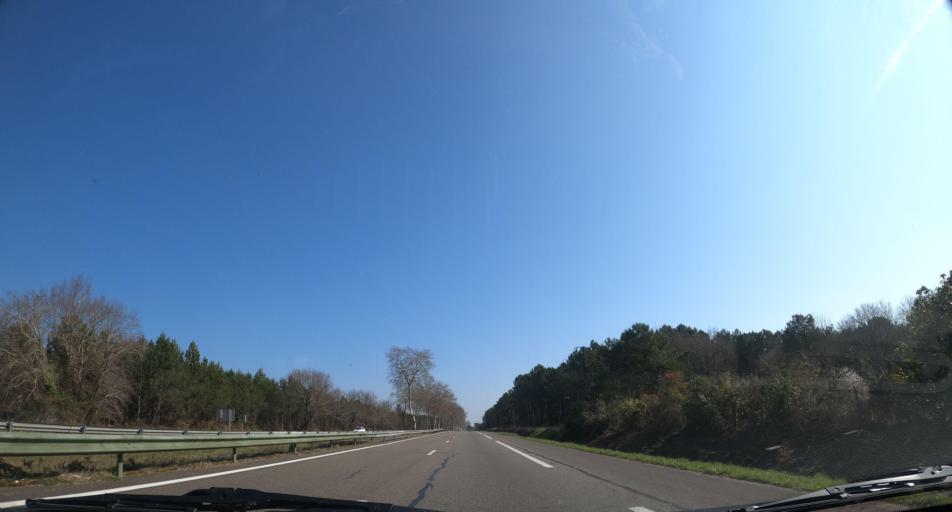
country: FR
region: Aquitaine
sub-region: Departement des Landes
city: Riviere-Saas-et-Gourby
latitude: 43.7113
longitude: -1.1525
